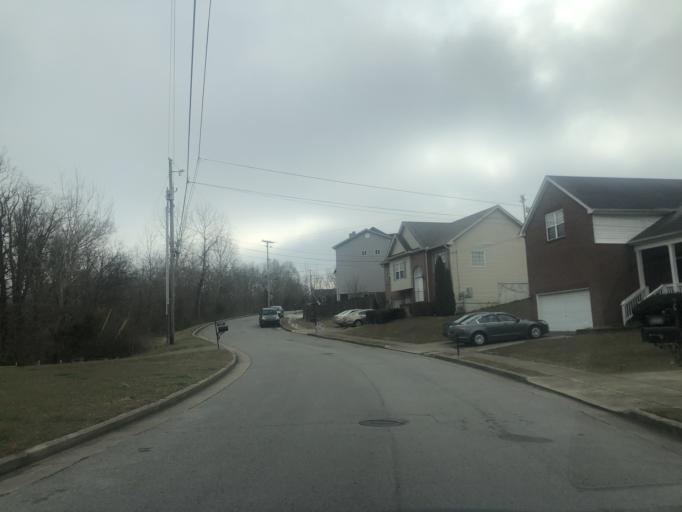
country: US
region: Tennessee
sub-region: Rutherford County
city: La Vergne
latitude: 36.0719
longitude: -86.6486
